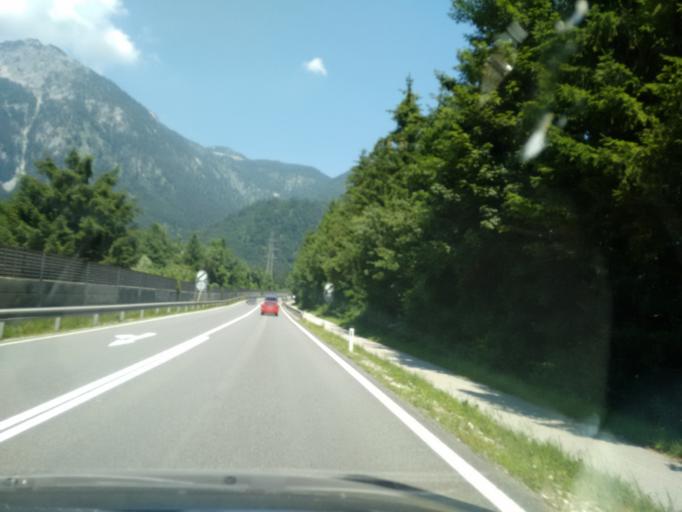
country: AT
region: Upper Austria
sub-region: Politischer Bezirk Gmunden
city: Ebensee
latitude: 47.7776
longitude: 13.7294
